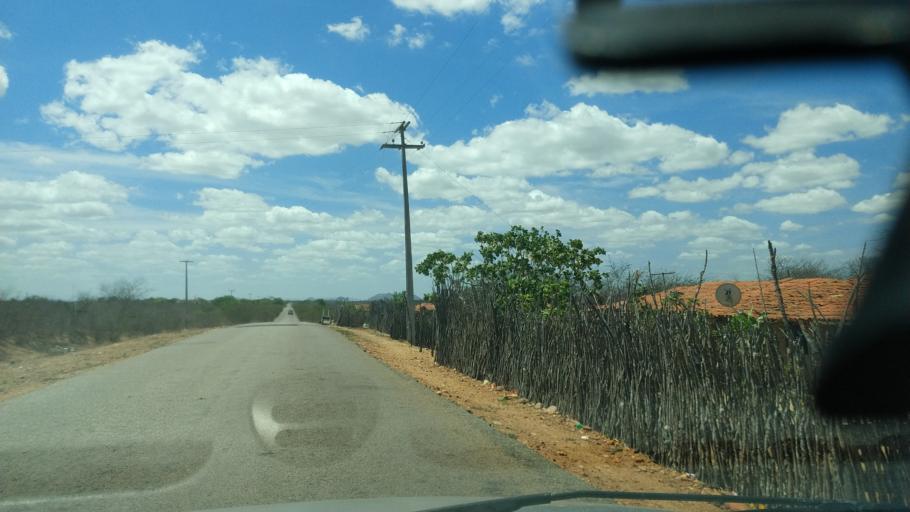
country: BR
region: Rio Grande do Norte
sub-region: Sao Paulo Do Potengi
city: Sao Paulo do Potengi
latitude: -5.9146
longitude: -35.7582
